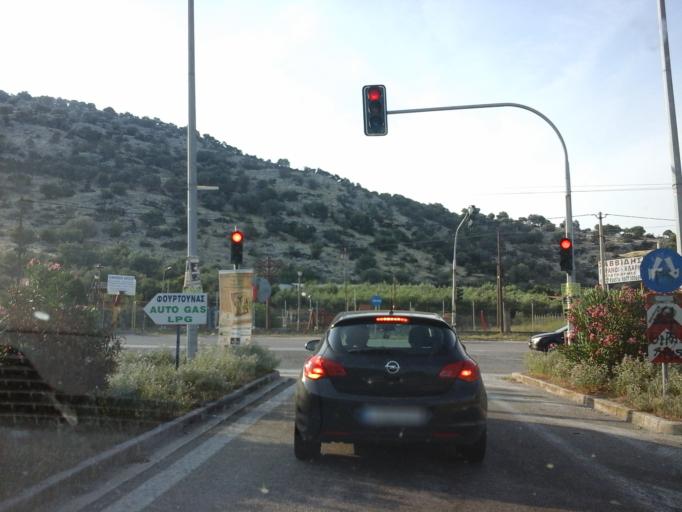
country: GR
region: East Macedonia and Thrace
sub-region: Nomos Kavalas
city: Nea Karvali
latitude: 40.9567
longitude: 24.4619
